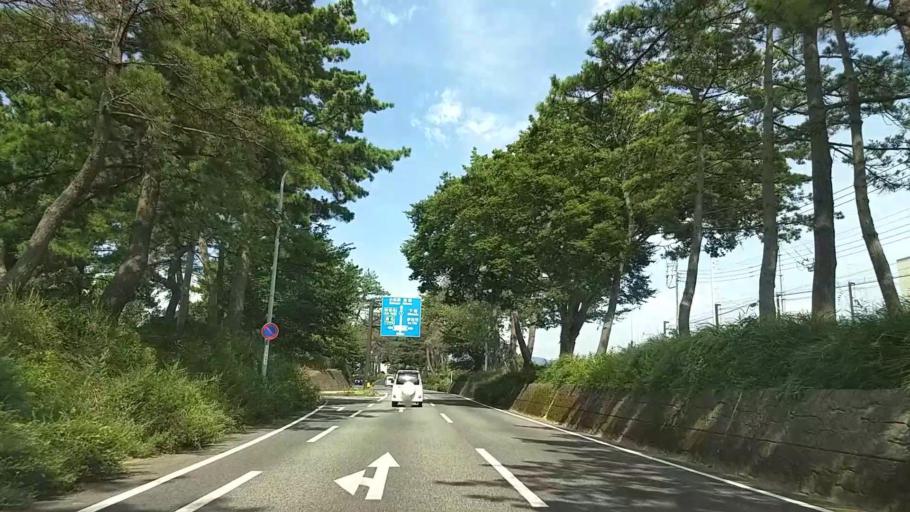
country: JP
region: Shizuoka
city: Mishima
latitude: 35.1270
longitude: 138.9394
